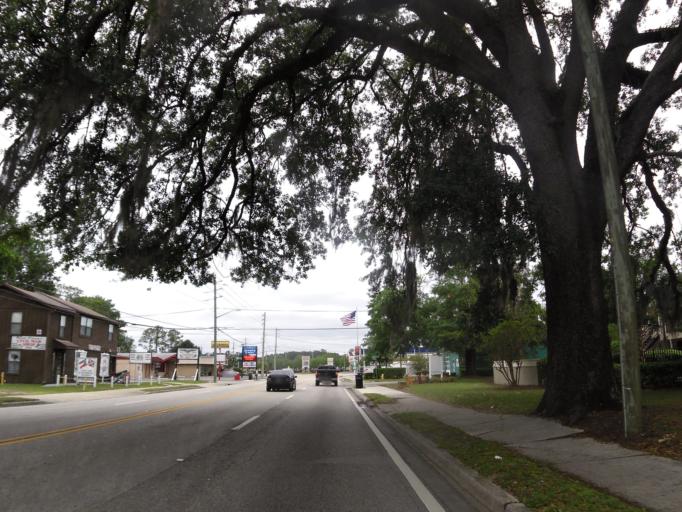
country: US
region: Florida
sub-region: Duval County
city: Jacksonville
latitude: 30.2582
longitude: -81.6261
